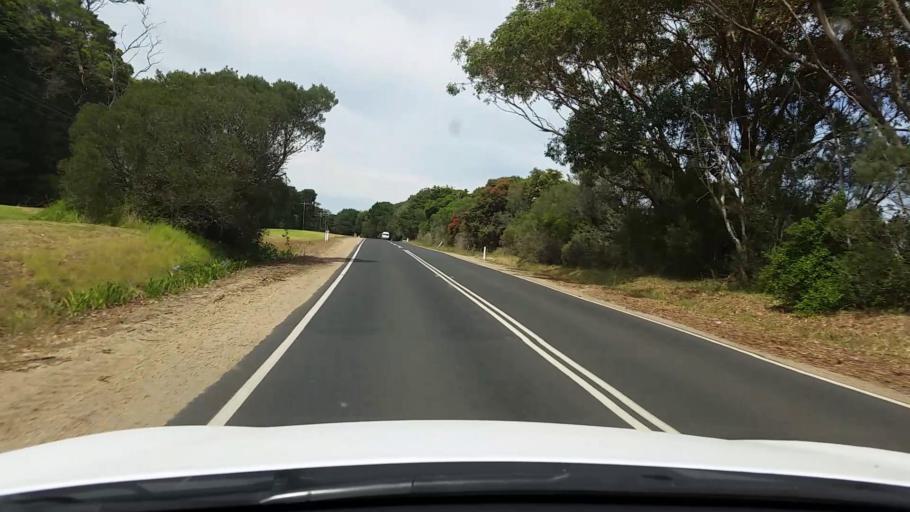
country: AU
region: Victoria
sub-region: Mornington Peninsula
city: Merricks
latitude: -38.4533
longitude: 145.0203
